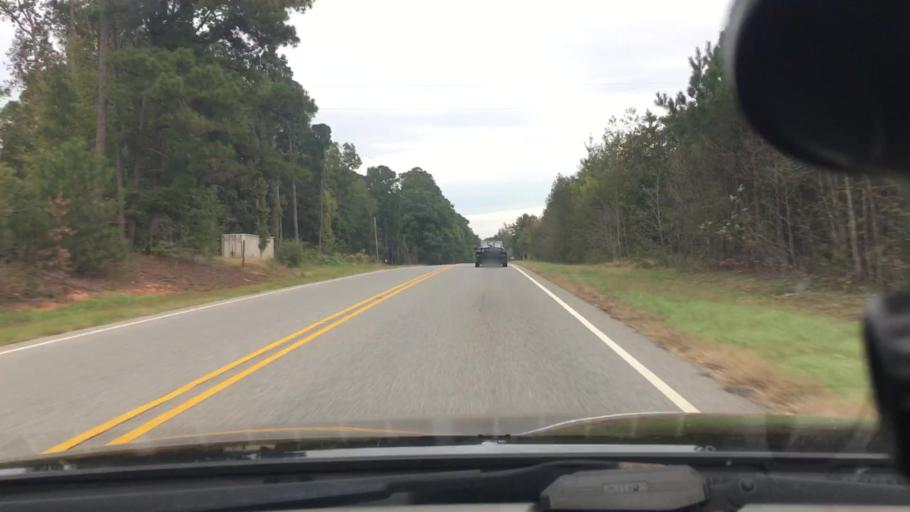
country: US
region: North Carolina
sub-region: Montgomery County
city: Biscoe
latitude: 35.3604
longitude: -79.7100
